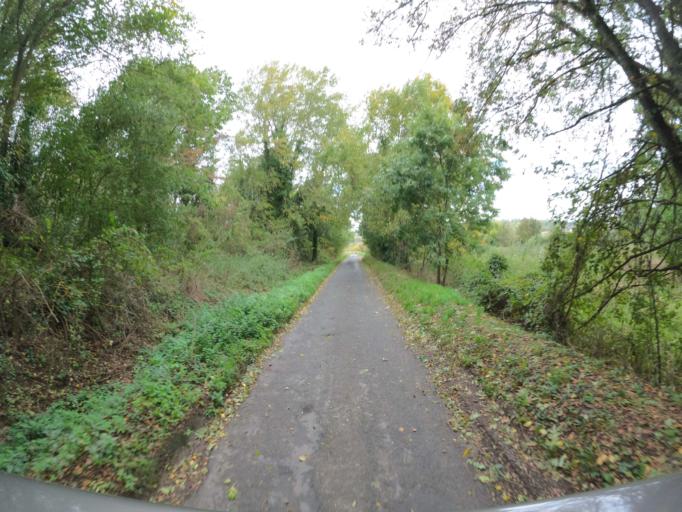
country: FR
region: Ile-de-France
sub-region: Departement de Seine-et-Marne
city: Montry
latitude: 48.8728
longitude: 2.8315
